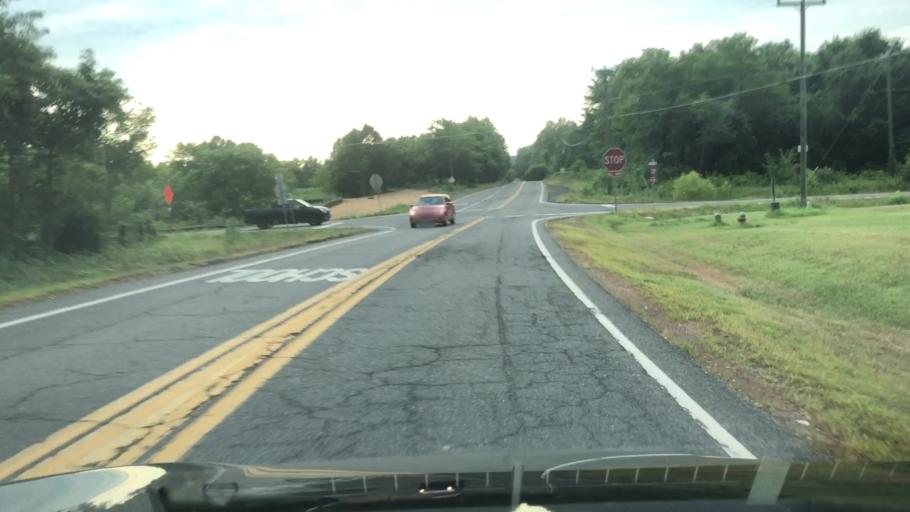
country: US
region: Virginia
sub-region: Fauquier County
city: New Baltimore
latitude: 38.7593
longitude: -77.6980
